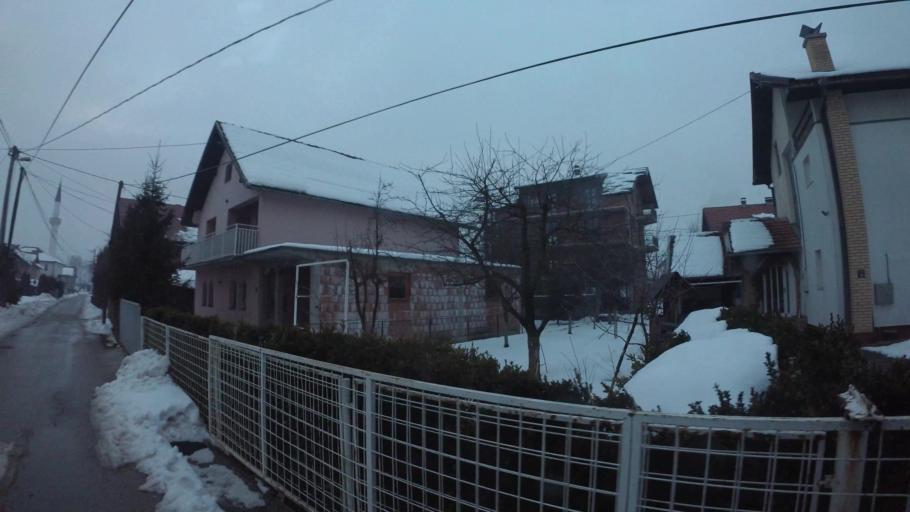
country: BA
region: Federation of Bosnia and Herzegovina
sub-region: Kanton Sarajevo
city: Sarajevo
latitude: 43.8516
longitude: 18.2951
